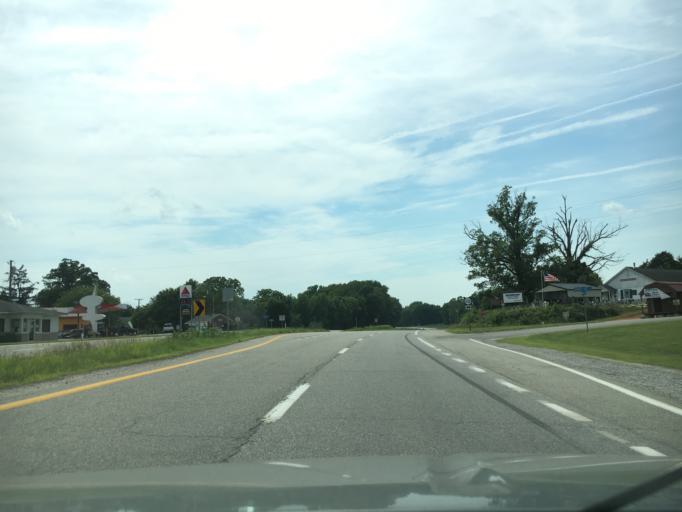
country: US
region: Virginia
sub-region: Prince Edward County
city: Hampden Sydney
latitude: 37.1052
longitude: -78.3611
